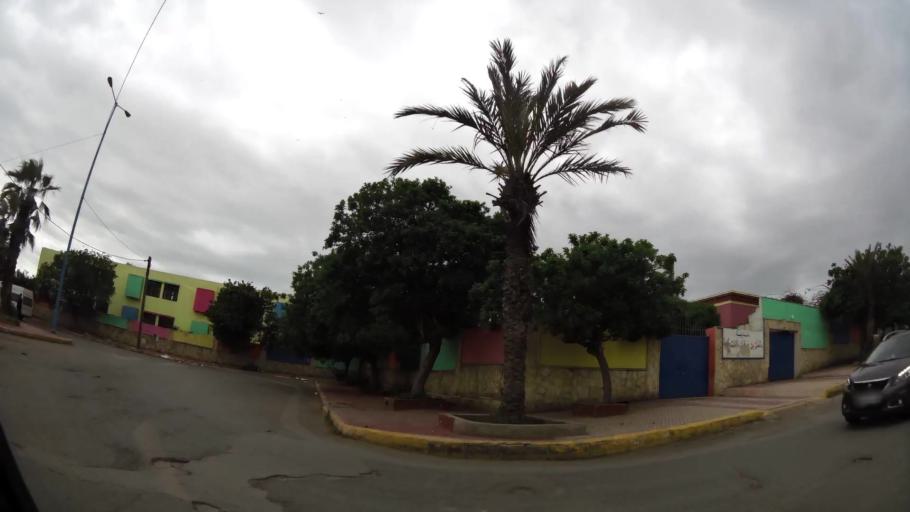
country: MA
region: Grand Casablanca
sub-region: Mediouna
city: Tit Mellil
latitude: 33.5574
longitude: -7.5375
